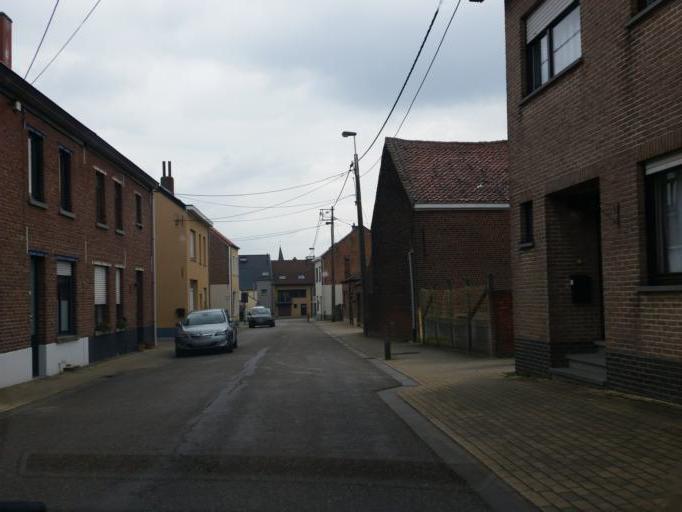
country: BE
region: Flanders
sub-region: Provincie Vlaams-Brabant
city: Bertem
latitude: 50.8799
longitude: 4.5884
